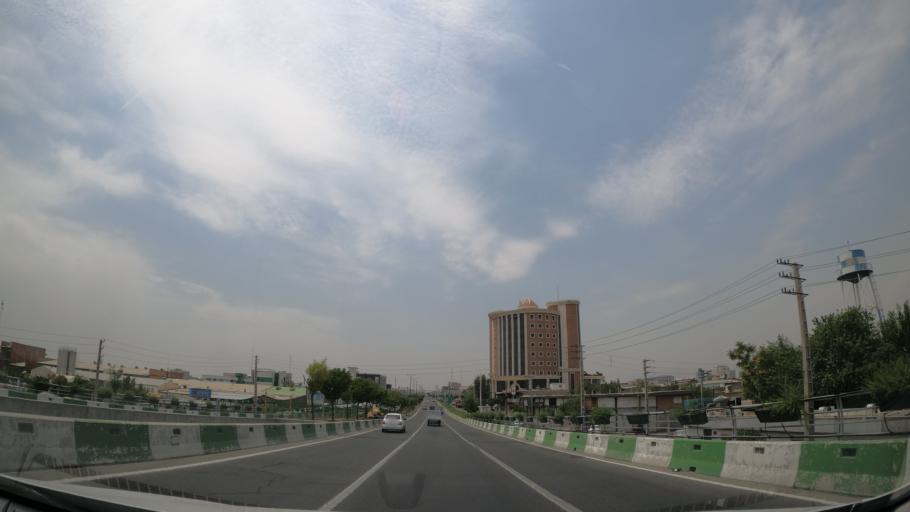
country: IR
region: Tehran
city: Tehran
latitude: 35.6758
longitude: 51.3068
